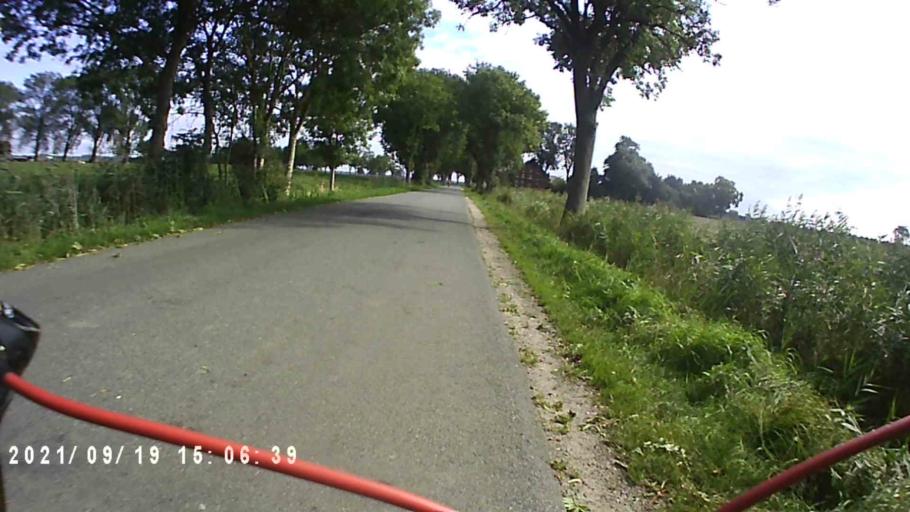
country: DE
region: Lower Saxony
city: Bunde
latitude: 53.1707
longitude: 7.2123
